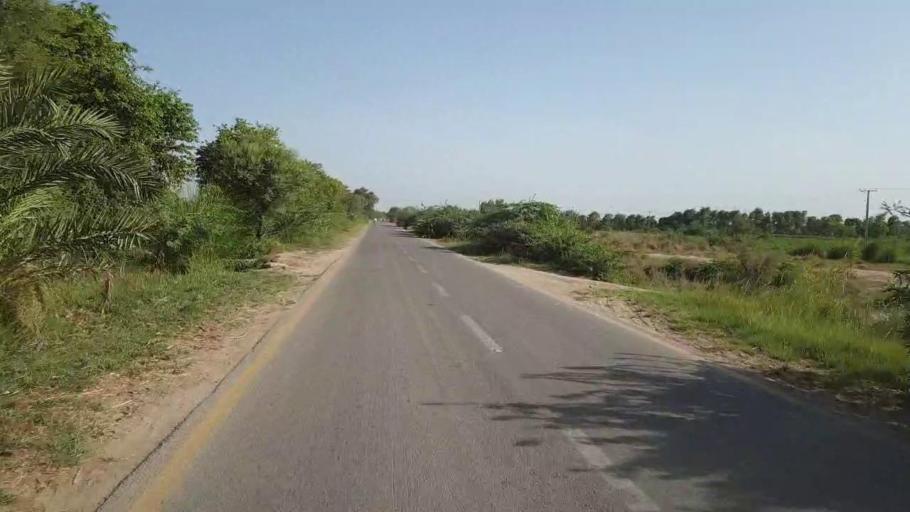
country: PK
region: Sindh
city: Daur
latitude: 26.4572
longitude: 68.4507
